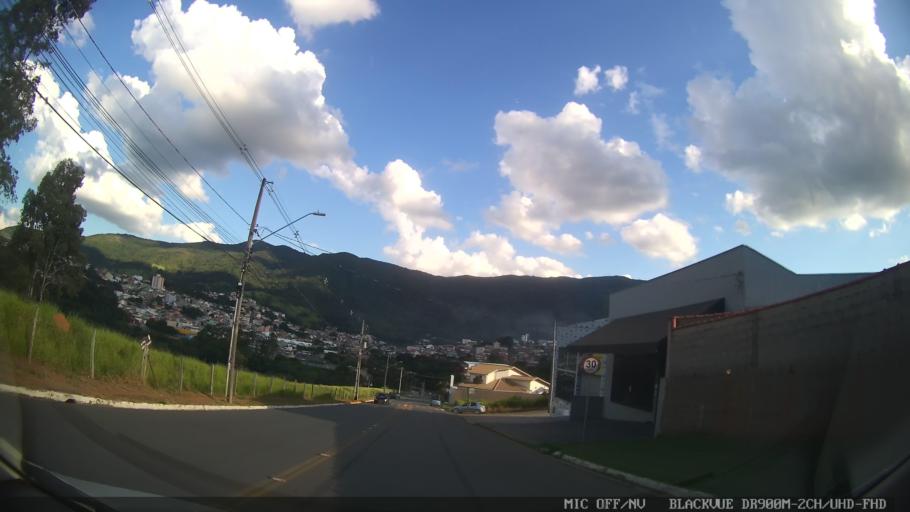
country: BR
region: Minas Gerais
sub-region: Extrema
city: Extrema
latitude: -22.8536
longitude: -46.3290
